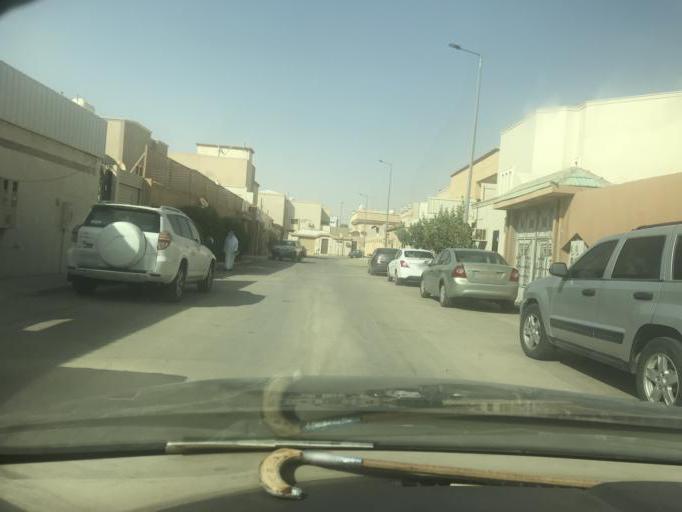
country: SA
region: Ar Riyad
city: Riyadh
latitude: 24.7372
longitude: 46.7797
